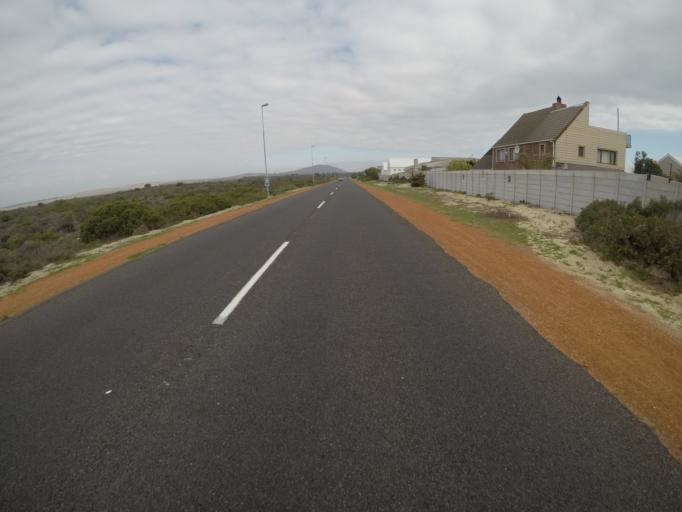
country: ZA
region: Western Cape
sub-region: City of Cape Town
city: Atlantis
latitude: -33.7026
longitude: 18.4457
